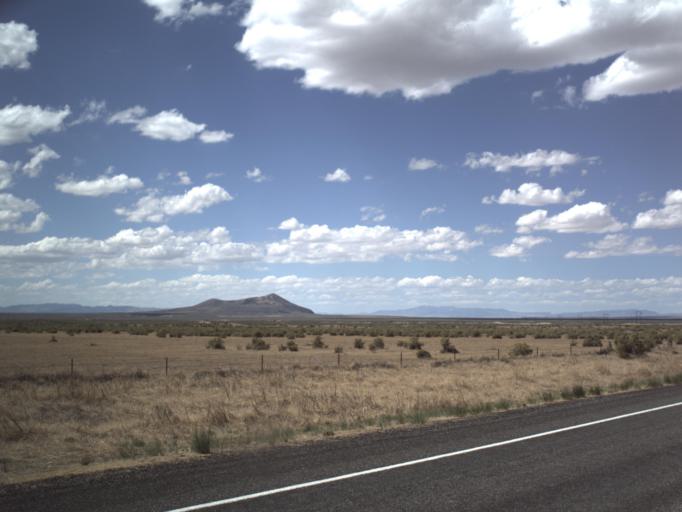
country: US
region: Utah
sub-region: Millard County
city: Fillmore
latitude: 39.1510
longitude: -112.3987
